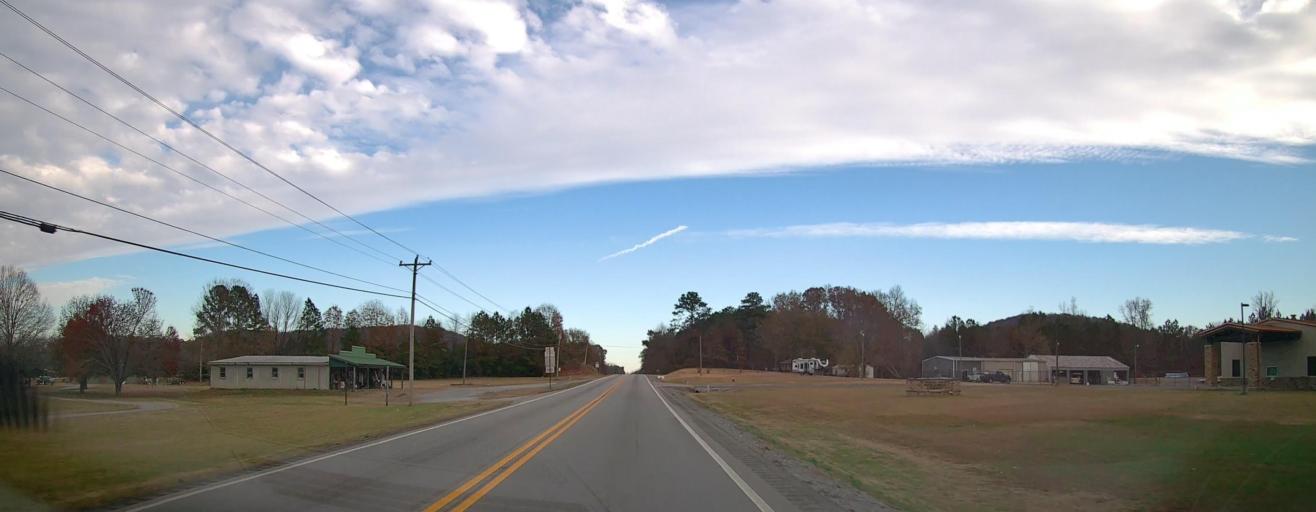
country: US
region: Alabama
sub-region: Morgan County
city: Priceville
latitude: 34.4446
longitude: -86.7539
